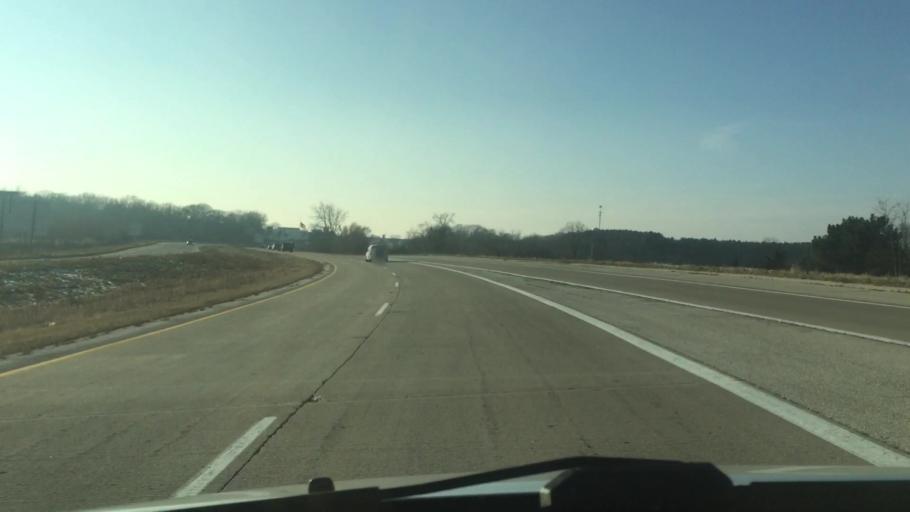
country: US
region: Wisconsin
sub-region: Waukesha County
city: Okauchee Lake
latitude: 43.1082
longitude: -88.4660
